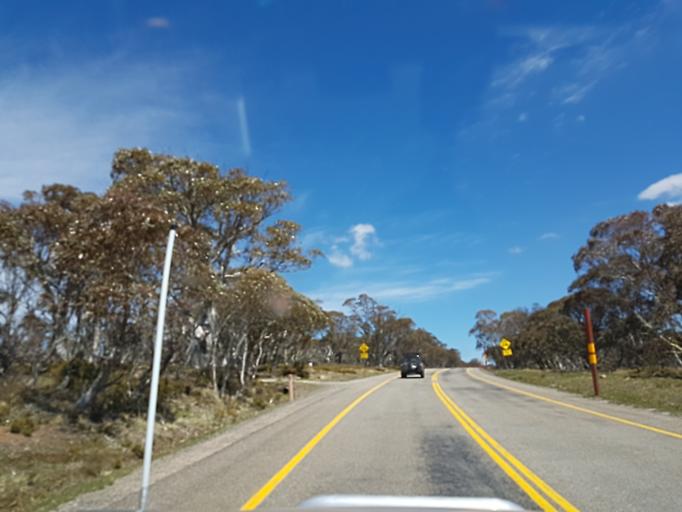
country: AU
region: Victoria
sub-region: Alpine
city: Mount Beauty
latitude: -37.0212
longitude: 147.2567
